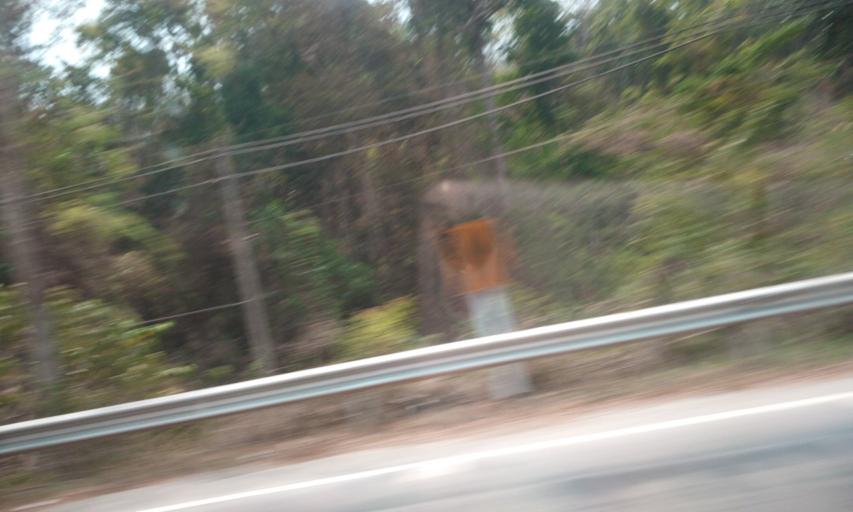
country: TH
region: Chiang Rai
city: Pa Daet
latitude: 19.6149
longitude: 100.0118
